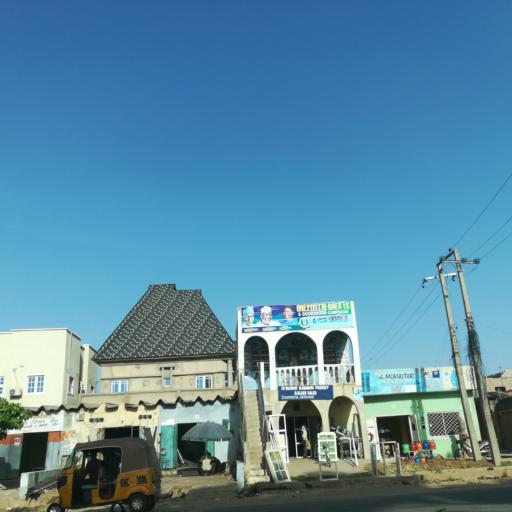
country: NG
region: Kano
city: Kano
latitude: 12.0221
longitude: 8.5027
